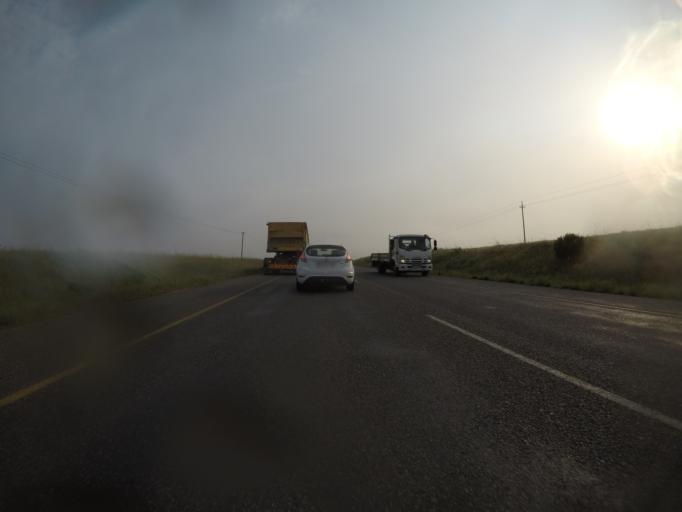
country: ZA
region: Western Cape
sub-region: City of Cape Town
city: Kraaifontein
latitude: -33.6559
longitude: 18.7085
